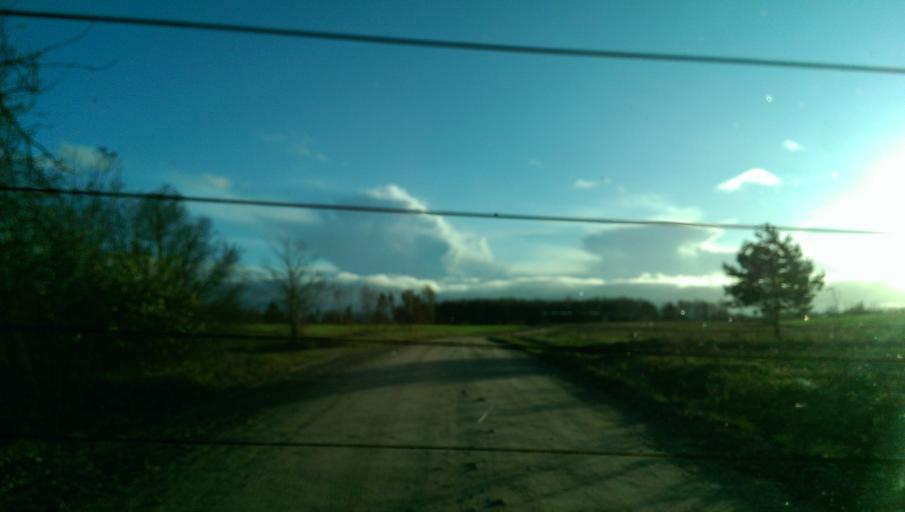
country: LV
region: Aizpute
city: Aizpute
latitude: 56.7443
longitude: 21.7473
